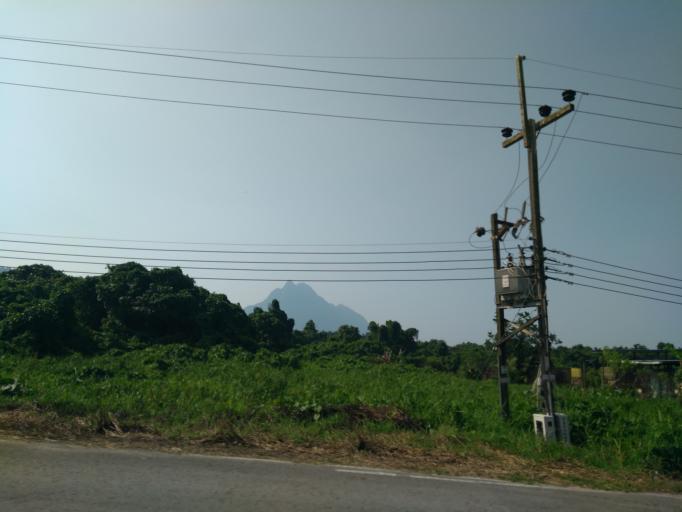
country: MY
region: Sarawak
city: Kuching
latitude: 1.6799
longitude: 110.3339
